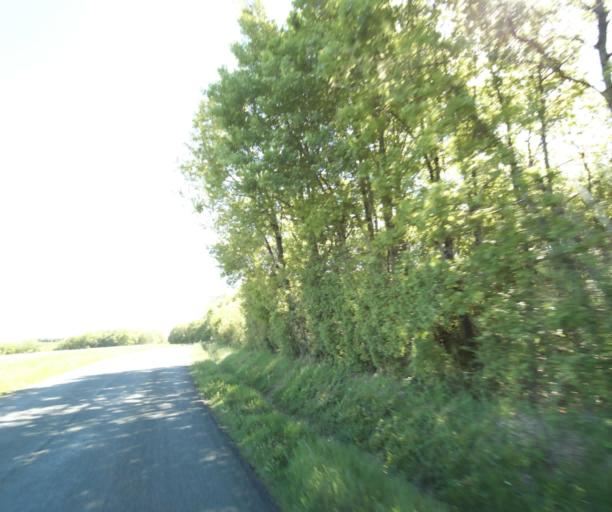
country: FR
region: Poitou-Charentes
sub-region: Departement de la Charente-Maritime
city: Bussac-sur-Charente
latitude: 45.8067
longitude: -0.6632
